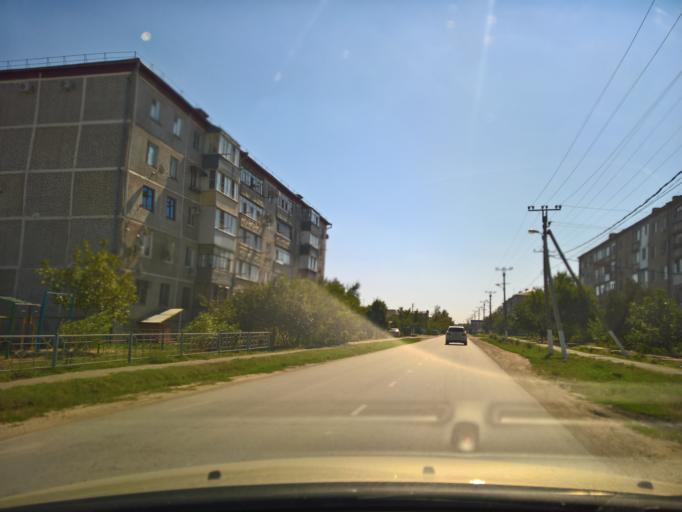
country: RU
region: Krasnodarskiy
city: Slavyansk-na-Kubani
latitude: 45.2658
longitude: 38.1086
